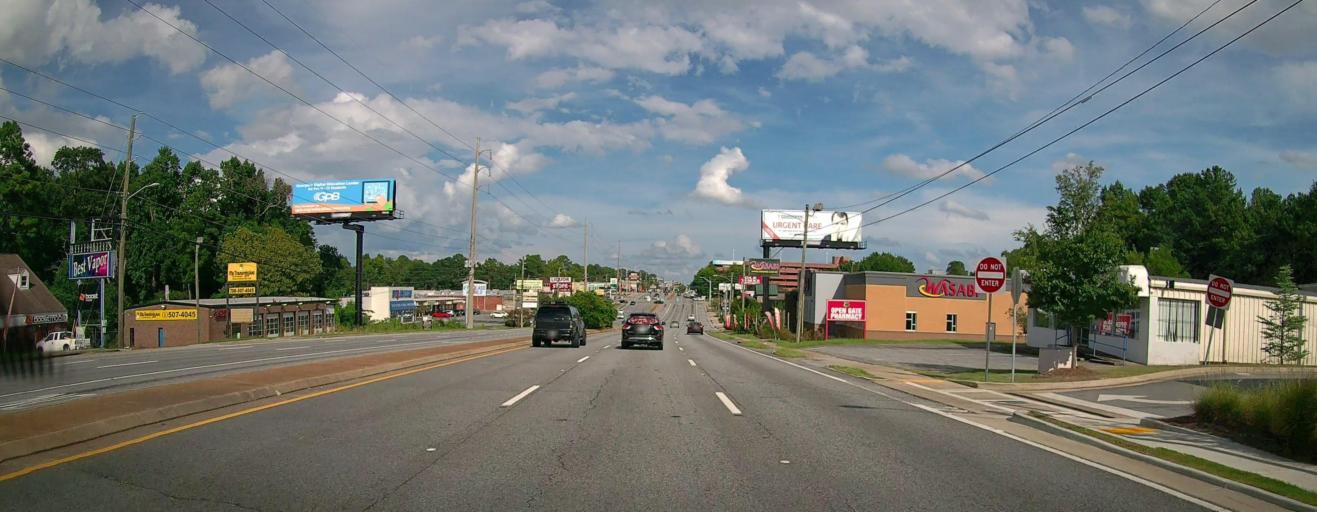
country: US
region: Alabama
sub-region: Russell County
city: Phenix City
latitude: 32.5070
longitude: -84.9663
